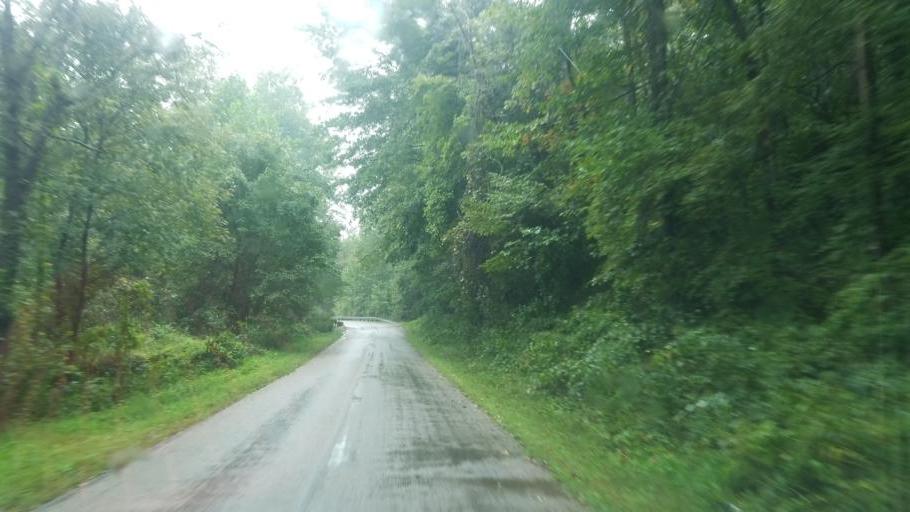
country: US
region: Kentucky
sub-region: Lewis County
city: Vanceburg
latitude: 38.7856
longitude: -83.2583
